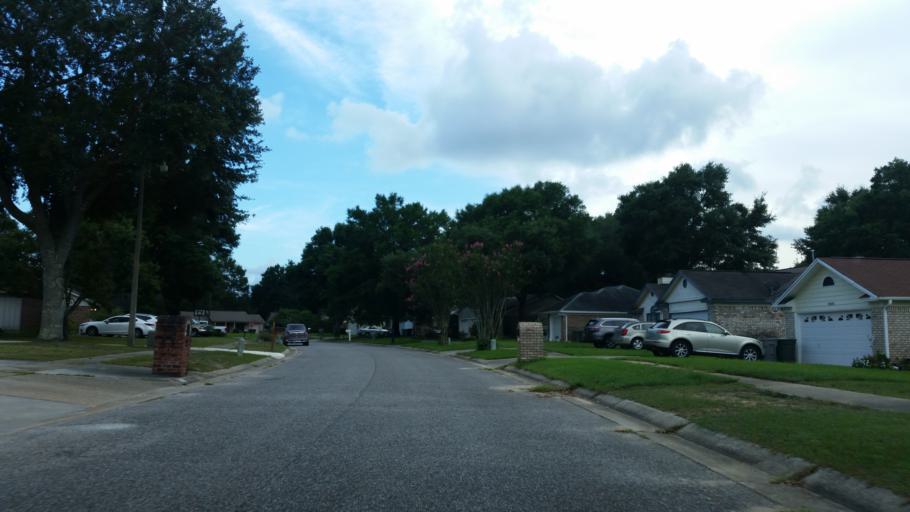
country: US
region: Florida
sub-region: Escambia County
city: Ferry Pass
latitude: 30.5054
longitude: -87.1705
